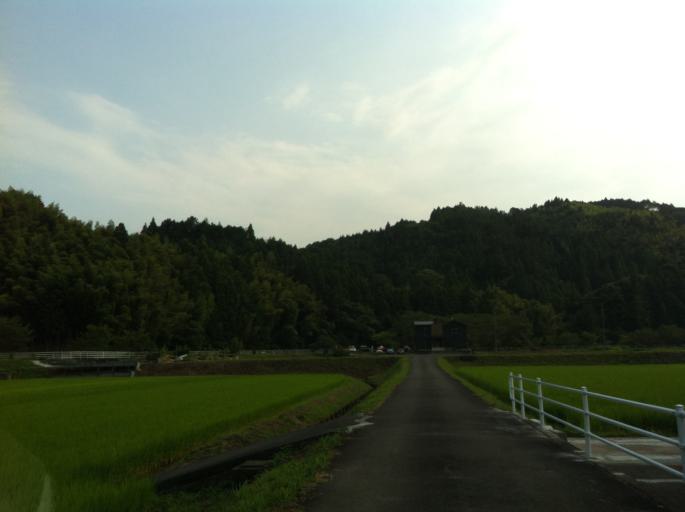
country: JP
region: Shizuoka
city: Fujieda
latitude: 34.9482
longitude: 138.2556
